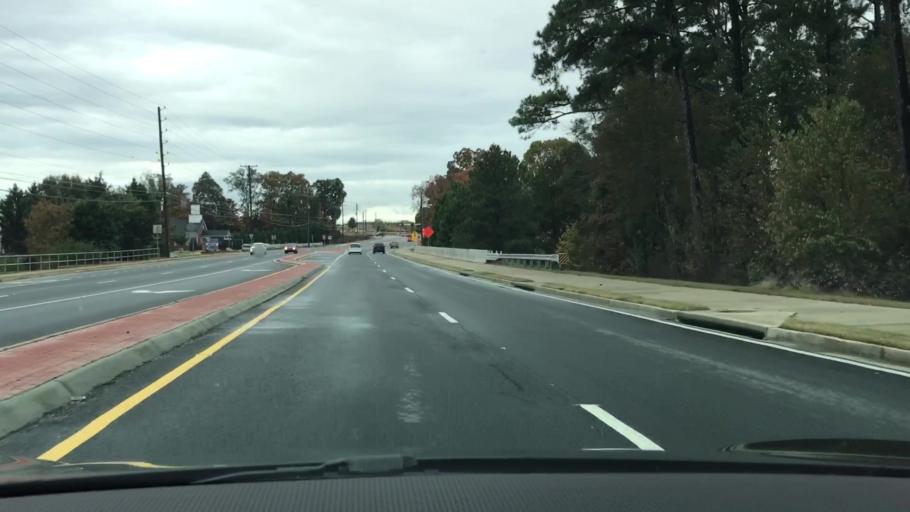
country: US
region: Georgia
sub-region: Fulton County
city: Johns Creek
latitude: 34.1090
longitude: -84.1491
